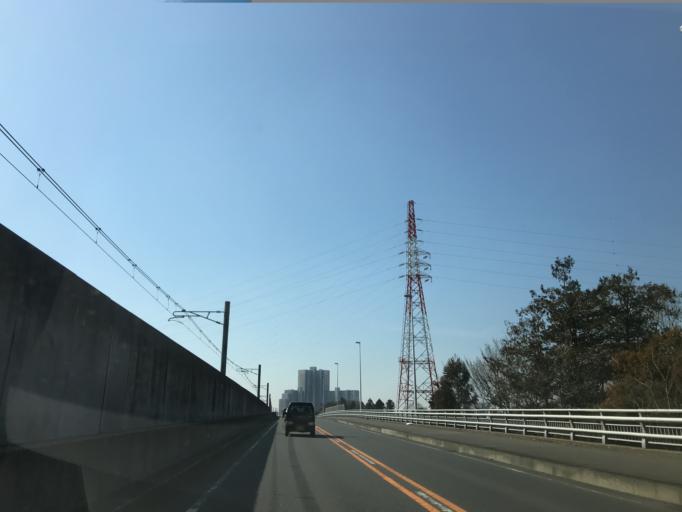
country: JP
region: Ibaraki
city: Moriya
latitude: 35.9603
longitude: 140.0040
